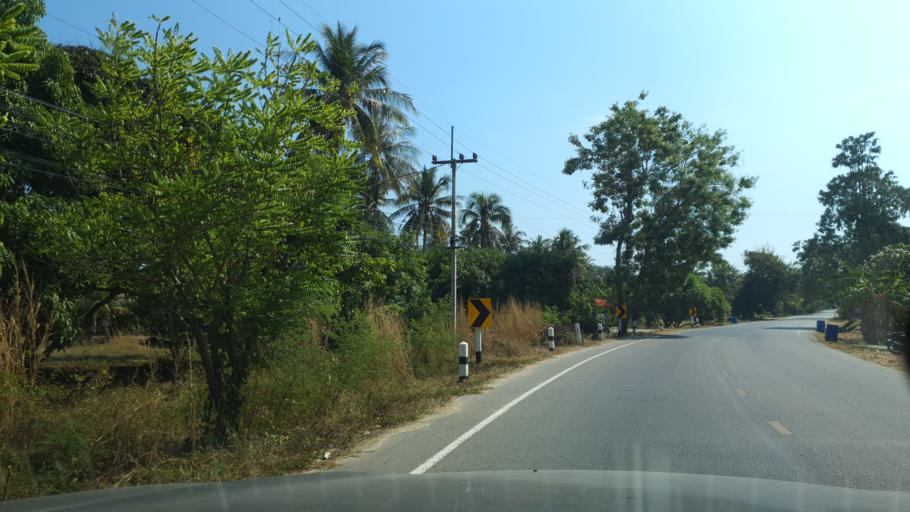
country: TH
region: Prachuap Khiri Khan
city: Sam Roi Yot
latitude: 12.2094
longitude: 99.9788
